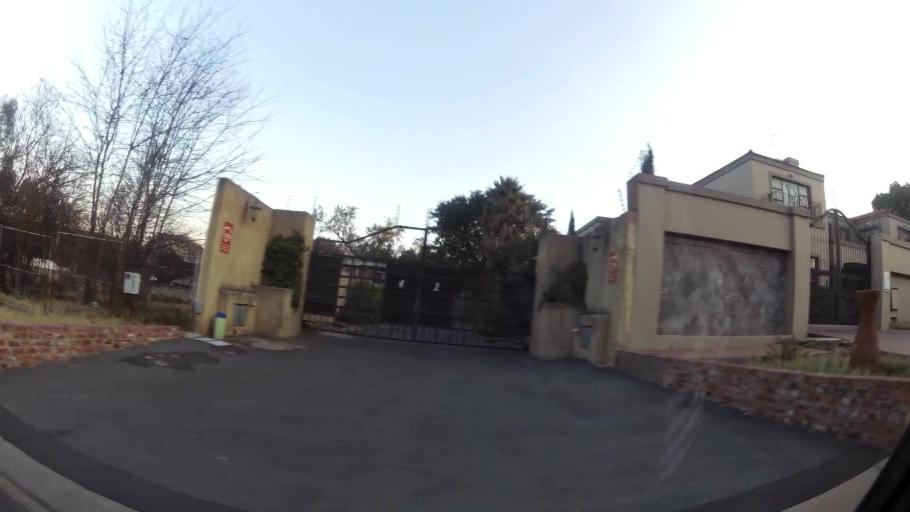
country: ZA
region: Gauteng
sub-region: City of Johannesburg Metropolitan Municipality
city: Diepsloot
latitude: -26.0190
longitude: 28.0361
